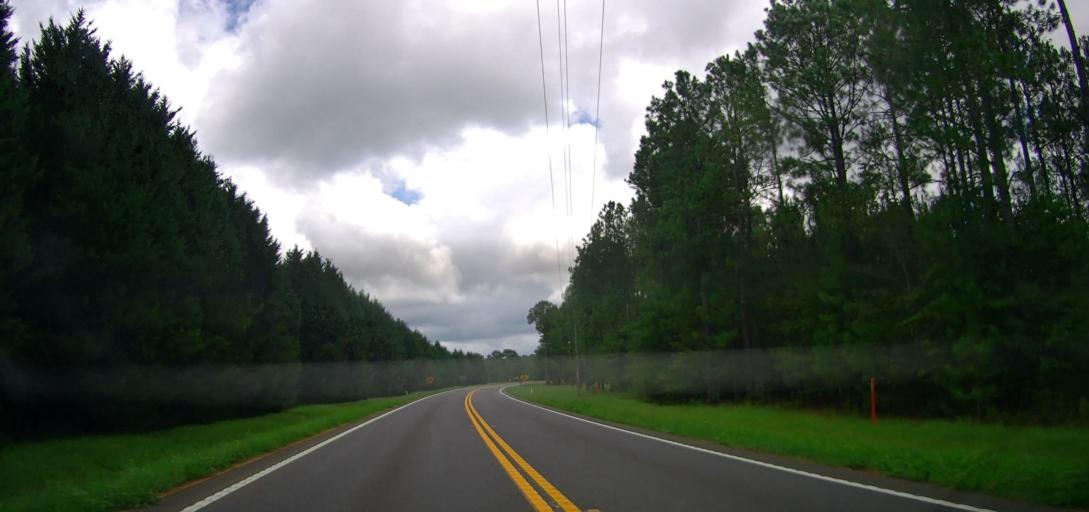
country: US
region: Georgia
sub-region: Pulaski County
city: Hawkinsville
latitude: 32.2317
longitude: -83.5088
